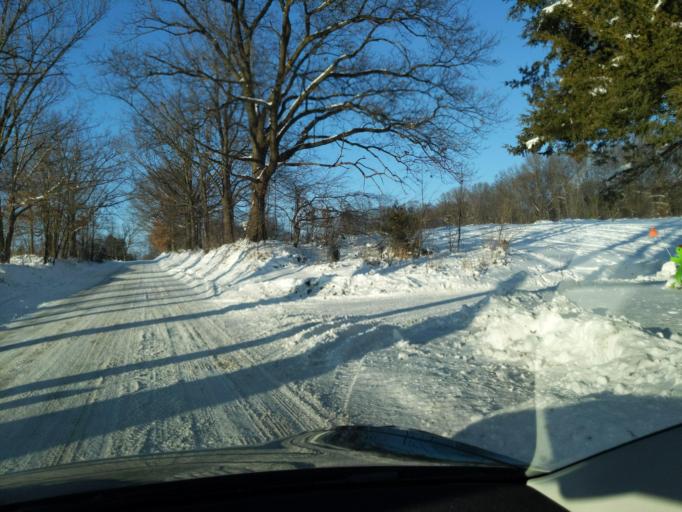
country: US
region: Michigan
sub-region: Ingham County
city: Stockbridge
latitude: 42.4685
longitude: -84.1193
